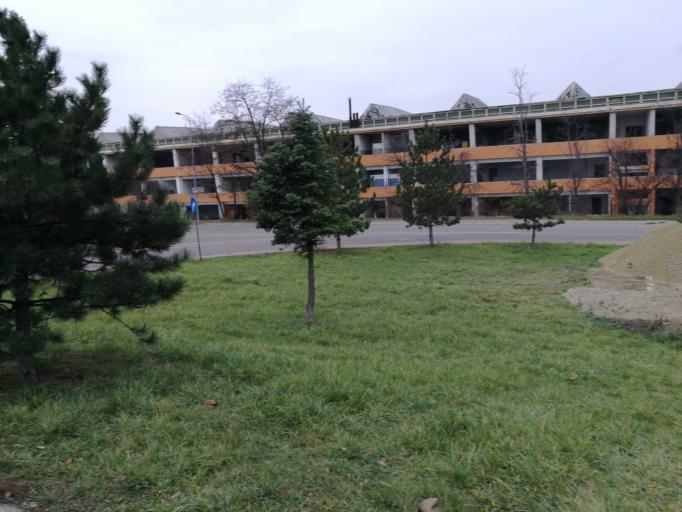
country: RO
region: Suceava
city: Suceava
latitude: 47.6665
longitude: 26.2711
